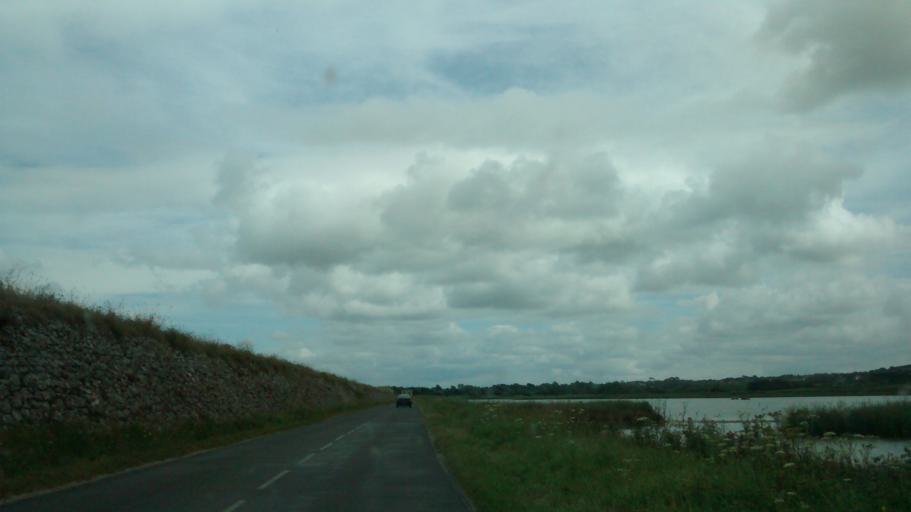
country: FR
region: Brittany
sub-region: Departement du Finistere
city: Guisseny
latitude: 48.6373
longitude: -4.4393
